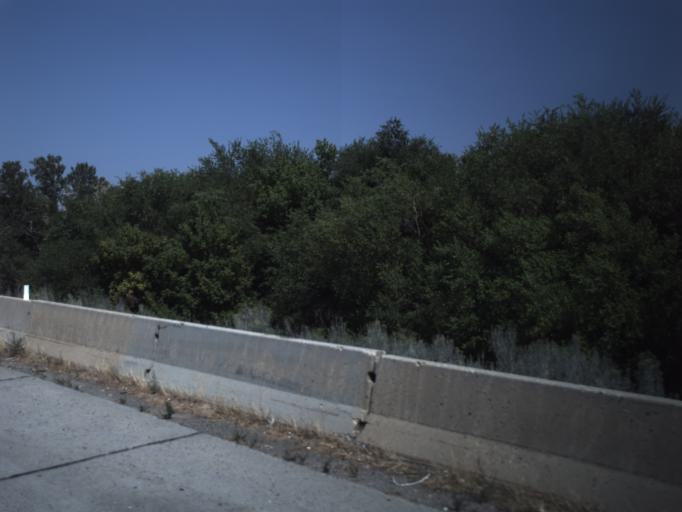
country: US
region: Utah
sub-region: Salt Lake County
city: Little Cottonwood Creek Valley
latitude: 40.6290
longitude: -111.8611
